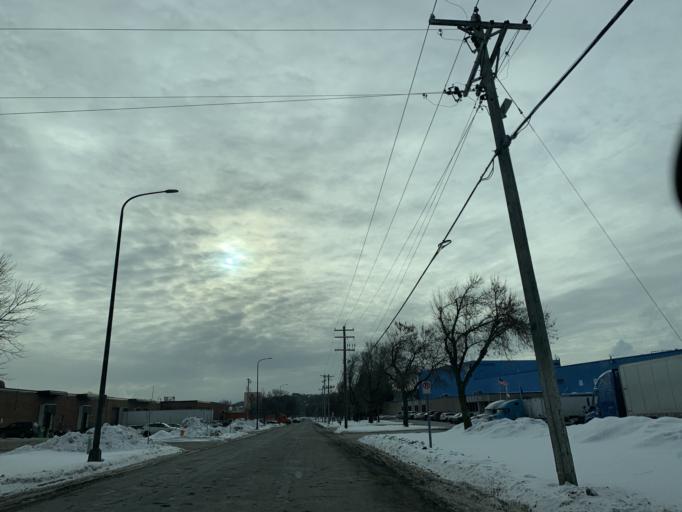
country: US
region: Minnesota
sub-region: Ramsey County
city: Saint Paul
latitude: 44.9415
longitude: -93.0817
